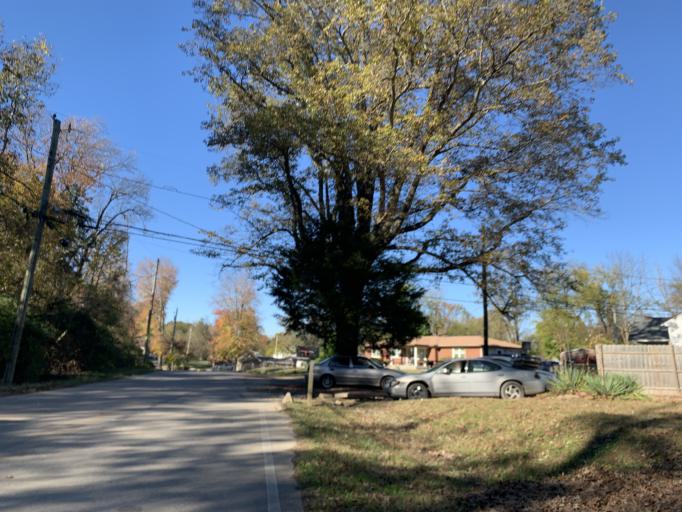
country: US
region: Kentucky
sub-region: Jefferson County
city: Pleasure Ridge Park
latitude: 38.1522
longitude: -85.8776
